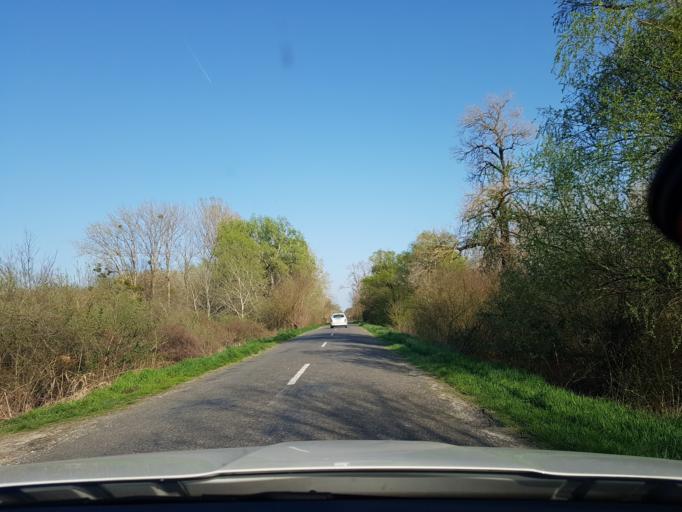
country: HU
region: Tolna
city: Bogyiszlo
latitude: 46.3306
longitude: 18.8333
